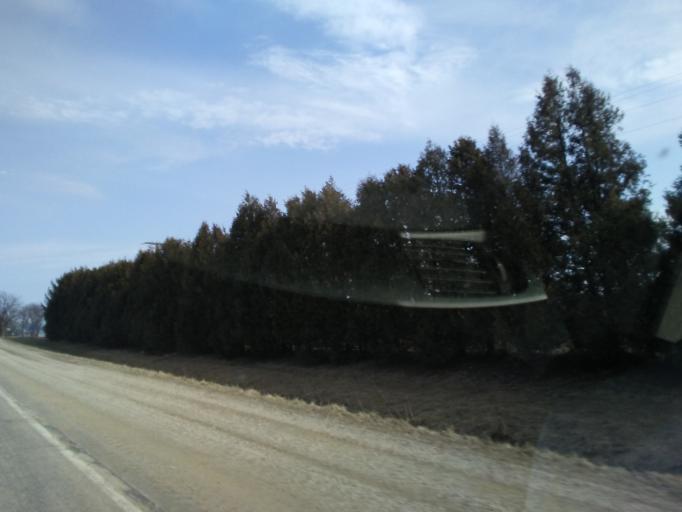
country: US
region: Iowa
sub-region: Clayton County
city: Monona
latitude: 43.1894
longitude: -91.3549
